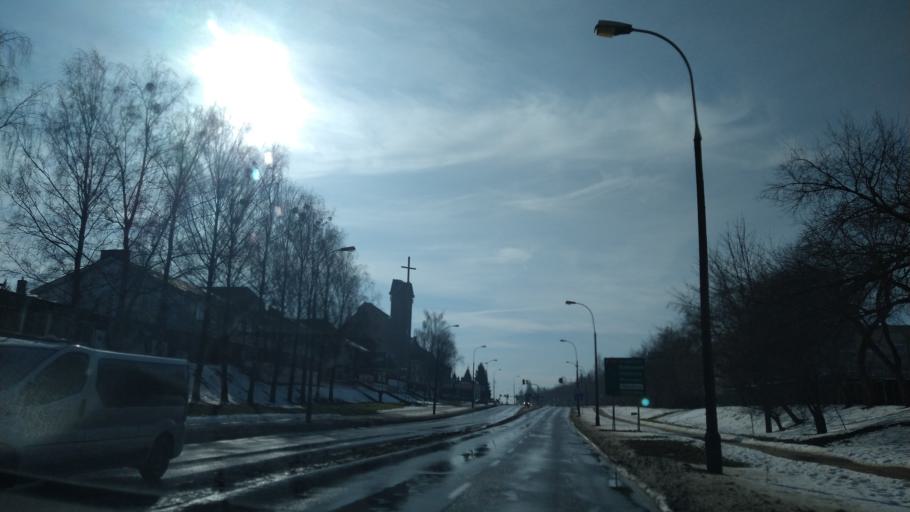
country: PL
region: Warmian-Masurian Voivodeship
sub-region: Powiat olsztynski
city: Olsztyn
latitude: 53.7675
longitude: 20.5058
